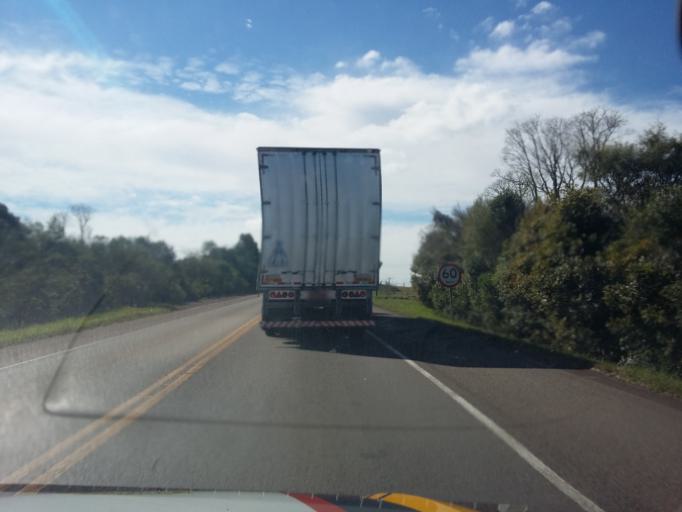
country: BR
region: Rio Grande do Sul
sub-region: Vacaria
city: Vacaria
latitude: -28.6048
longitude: -51.0400
